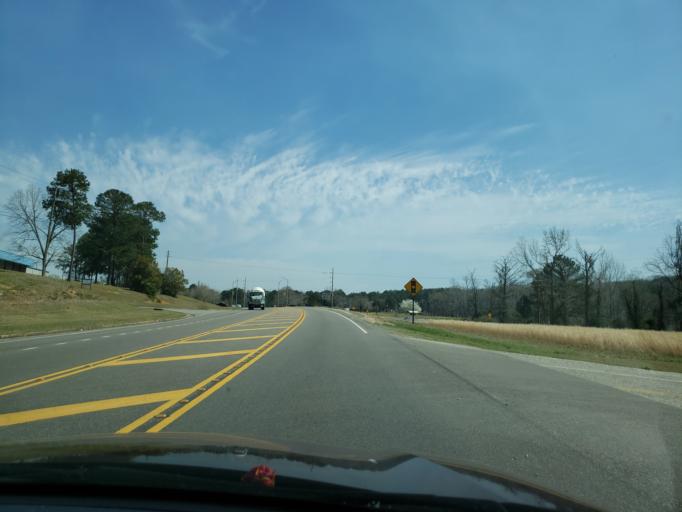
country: US
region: Alabama
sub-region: Elmore County
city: Wetumpka
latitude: 32.5518
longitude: -86.1794
